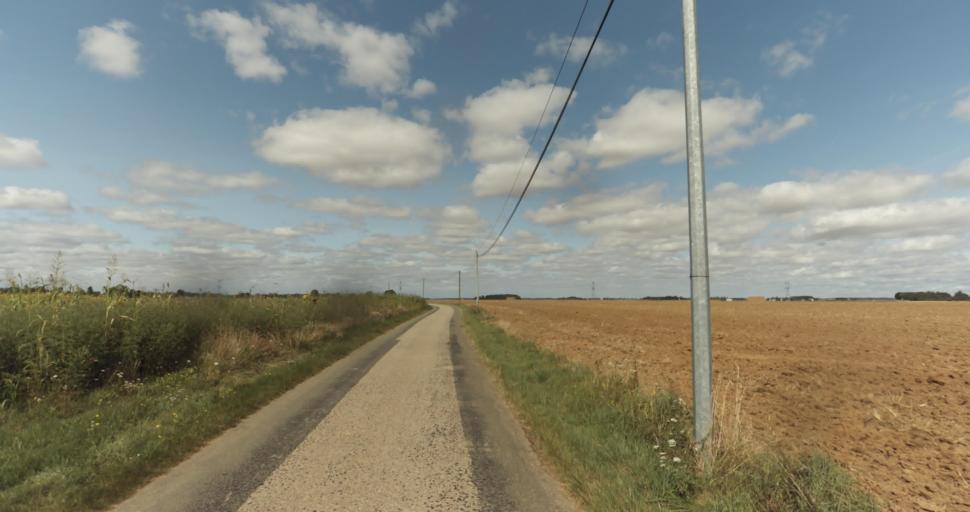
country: FR
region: Haute-Normandie
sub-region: Departement de l'Eure
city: Nonancourt
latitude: 48.8460
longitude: 1.1633
